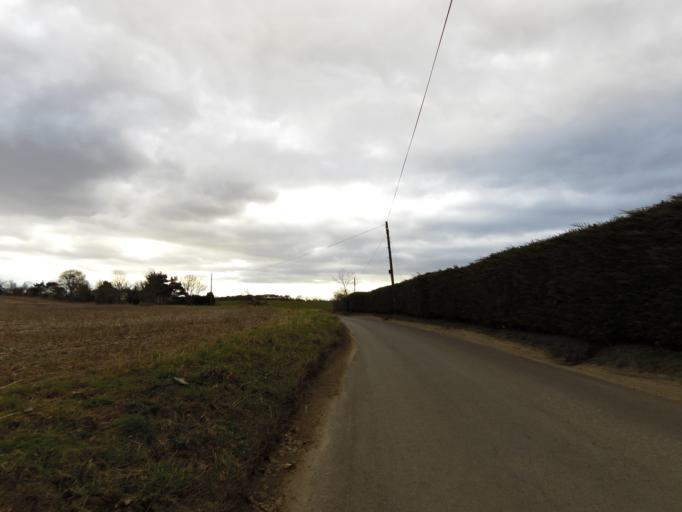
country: GB
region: England
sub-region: Suffolk
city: Woodbridge
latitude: 52.0236
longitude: 1.3001
